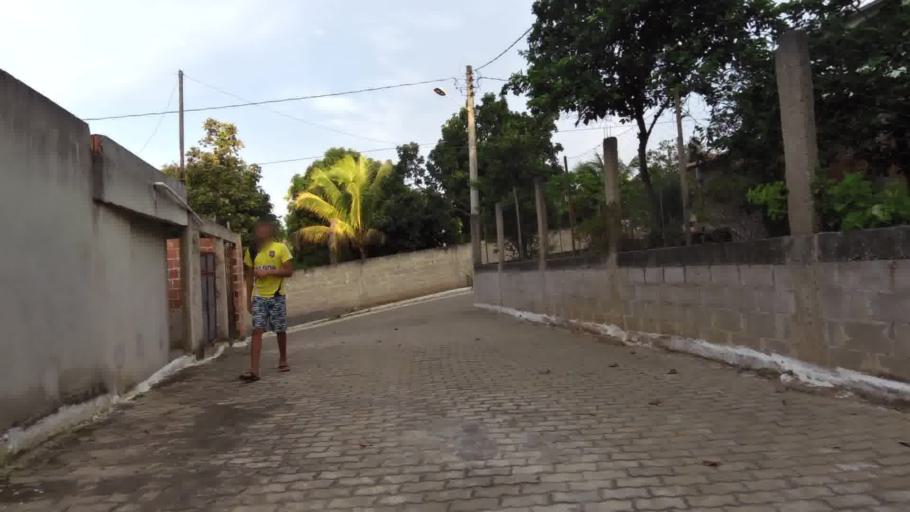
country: BR
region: Espirito Santo
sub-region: Piuma
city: Piuma
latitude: -20.8249
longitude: -40.7331
